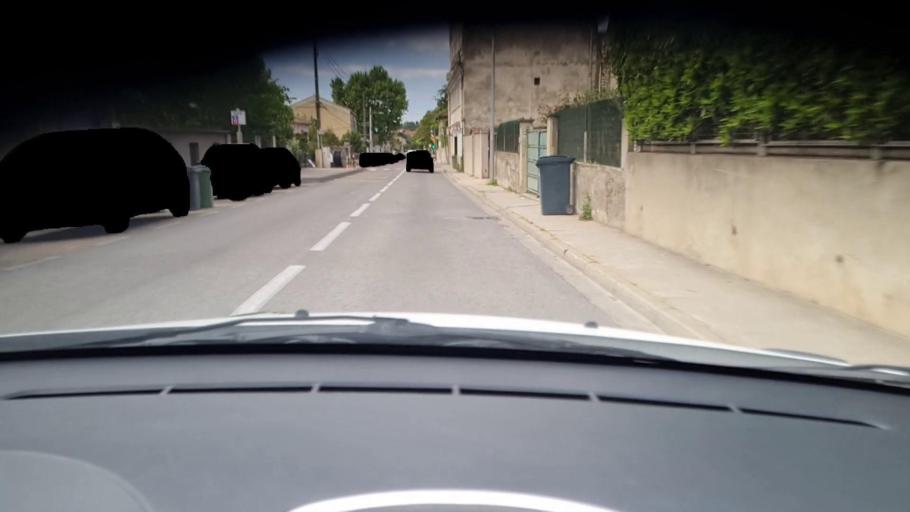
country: FR
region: Languedoc-Roussillon
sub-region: Departement du Gard
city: Nimes
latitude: 43.8525
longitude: 4.3780
